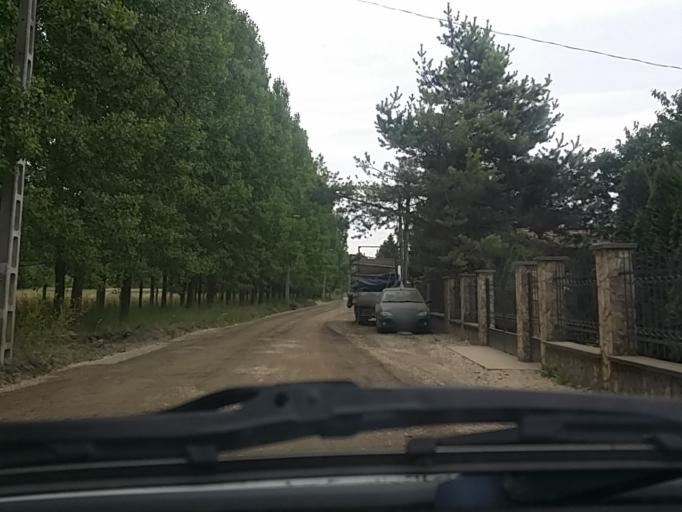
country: HU
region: Pest
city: Pilisborosjeno
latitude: 47.5991
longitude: 18.9734
